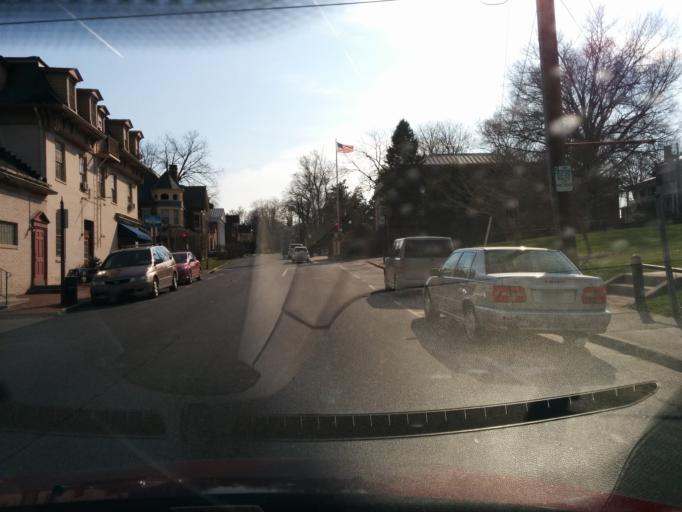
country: US
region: Virginia
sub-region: City of Lexington
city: Lexington
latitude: 37.7857
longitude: -79.4441
